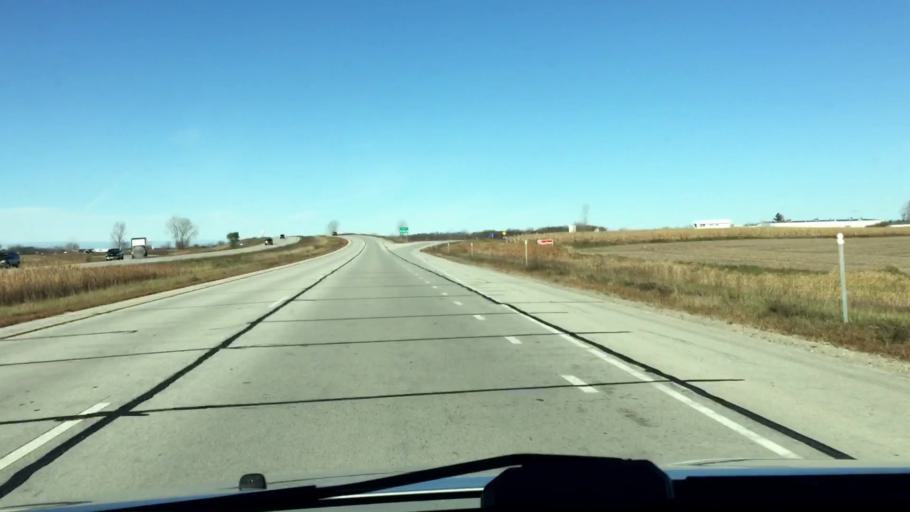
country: US
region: Wisconsin
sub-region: Brown County
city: Pulaski
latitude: 44.5950
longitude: -88.2143
